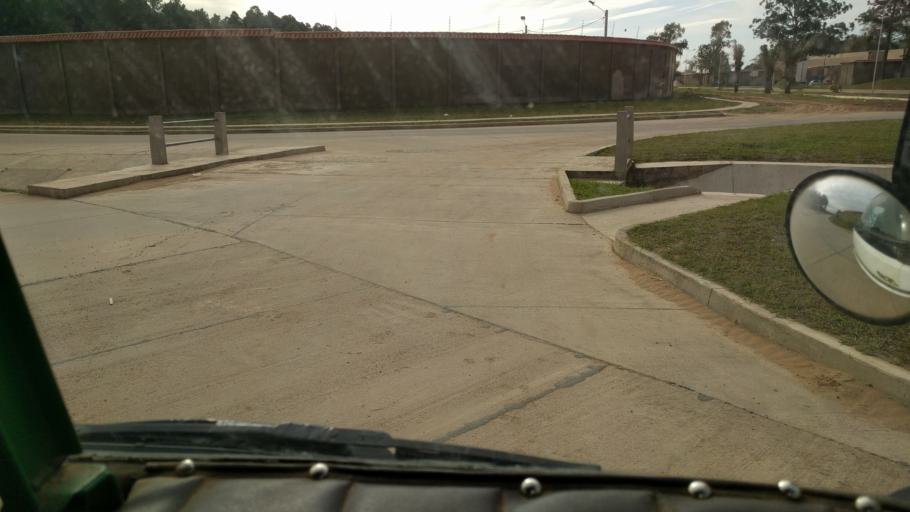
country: BO
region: Santa Cruz
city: Santa Cruz de la Sierra
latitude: -17.6797
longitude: -63.1429
